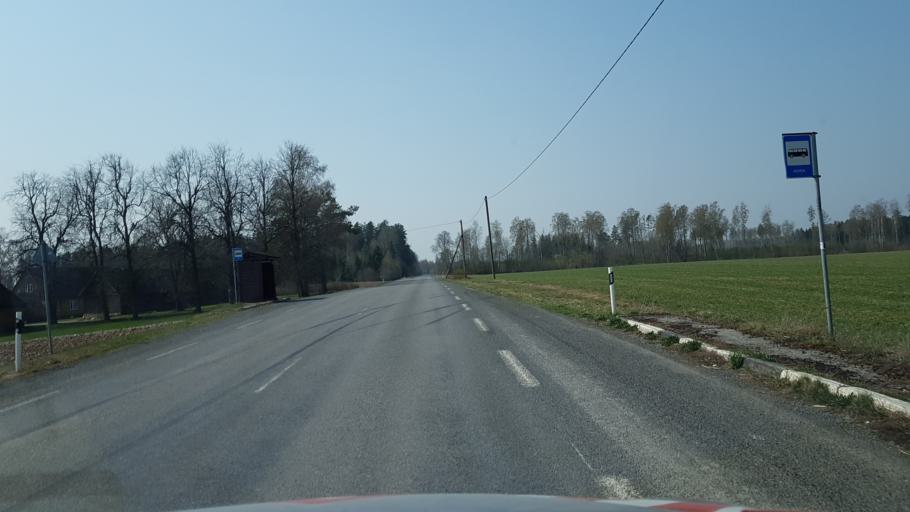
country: EE
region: Raplamaa
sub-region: Kehtna vald
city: Kehtna
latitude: 59.0040
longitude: 24.8860
